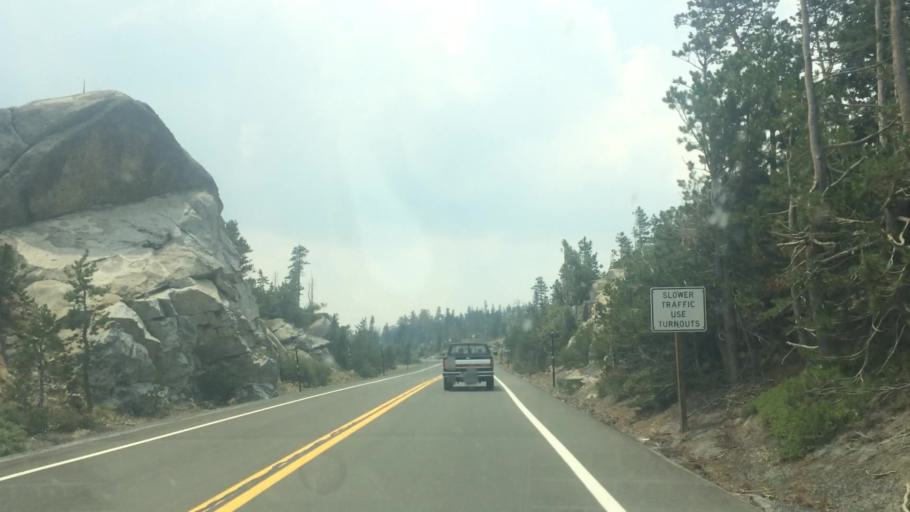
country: US
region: California
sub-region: El Dorado County
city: South Lake Tahoe
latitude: 38.6469
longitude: -120.1334
